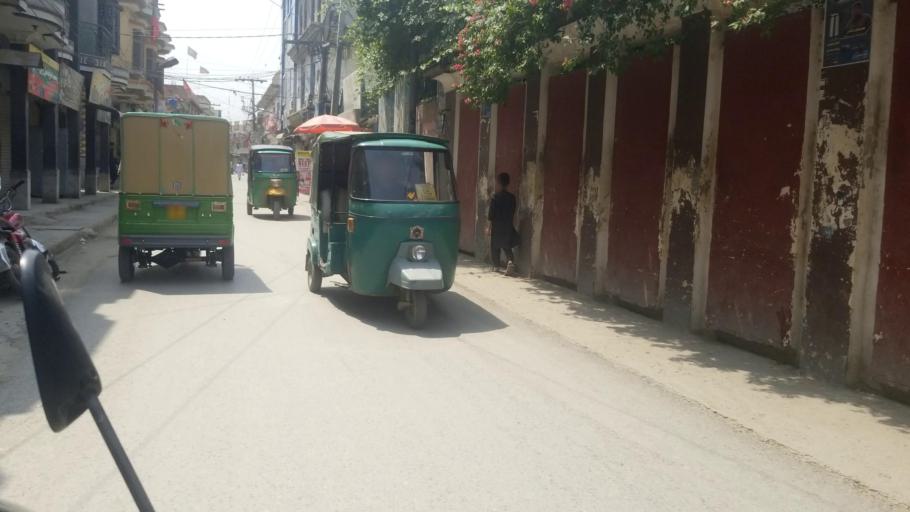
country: PK
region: Khyber Pakhtunkhwa
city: Peshawar
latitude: 34.0299
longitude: 71.5891
